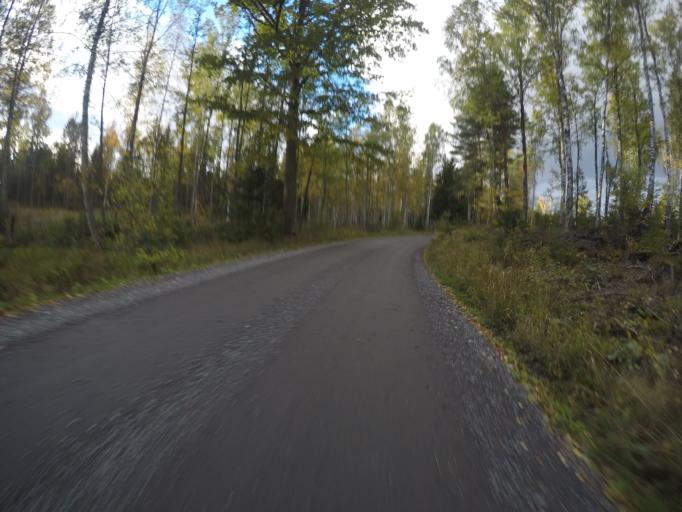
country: SE
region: Vaestmanland
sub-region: Arboga Kommun
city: Tyringe
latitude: 59.2948
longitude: 15.9839
